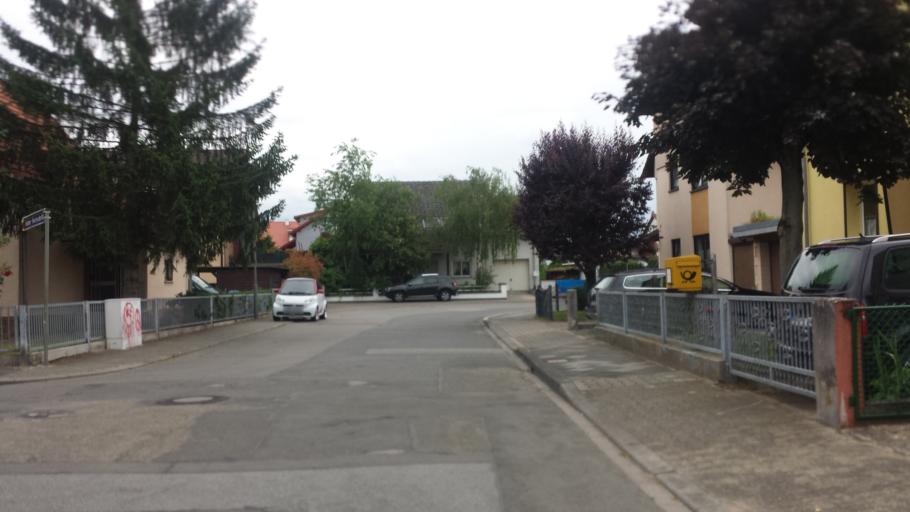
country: DE
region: Baden-Wuerttemberg
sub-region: Karlsruhe Region
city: Mannheim
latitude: 49.5177
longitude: 8.4944
